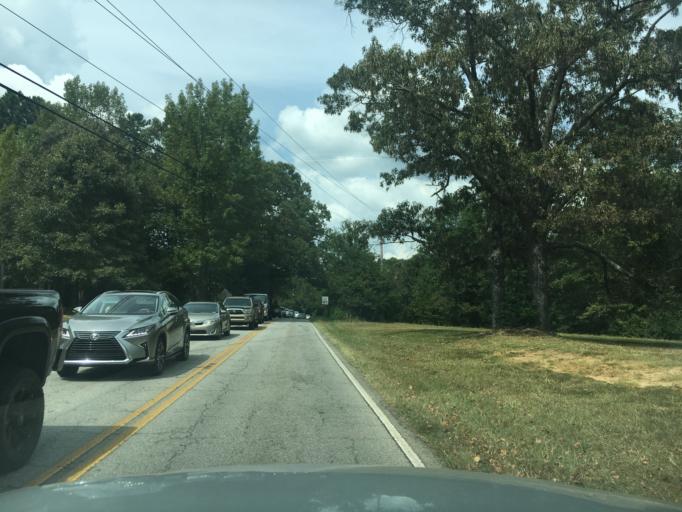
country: US
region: South Carolina
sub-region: Greenville County
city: Five Forks
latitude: 34.8233
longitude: -82.2287
